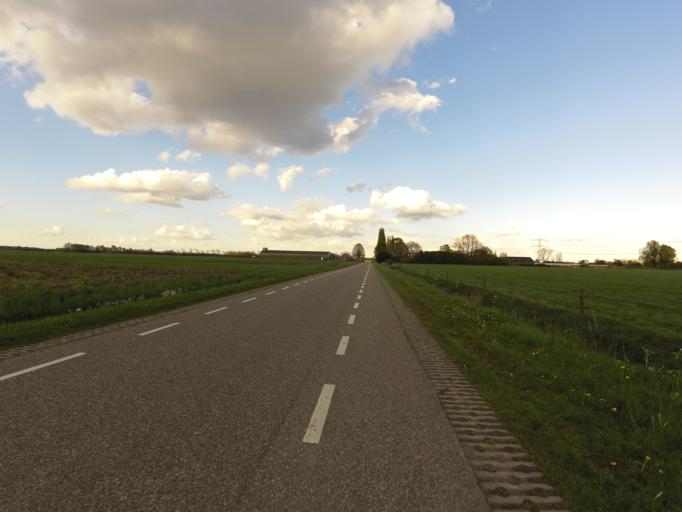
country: NL
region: Gelderland
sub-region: Gemeente Doesburg
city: Doesburg
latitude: 51.9713
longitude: 6.1230
